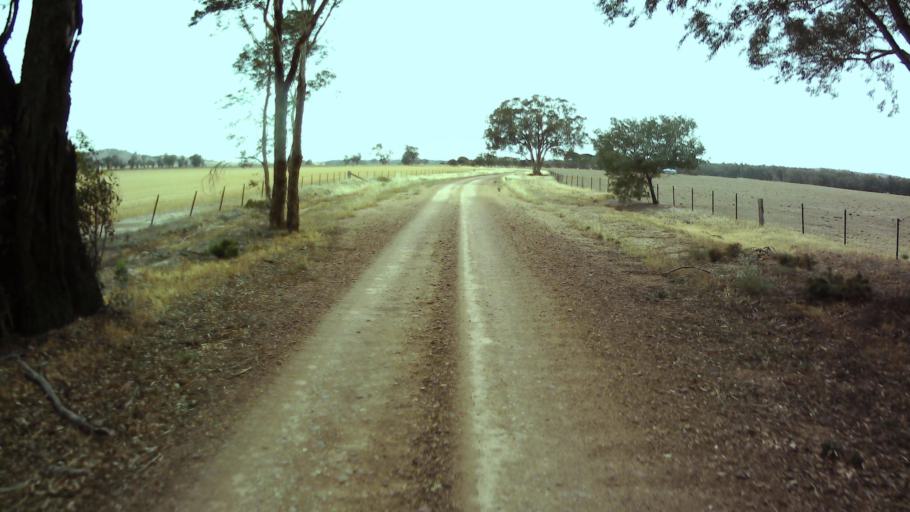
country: AU
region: New South Wales
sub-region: Weddin
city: Grenfell
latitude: -33.9178
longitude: 148.2874
